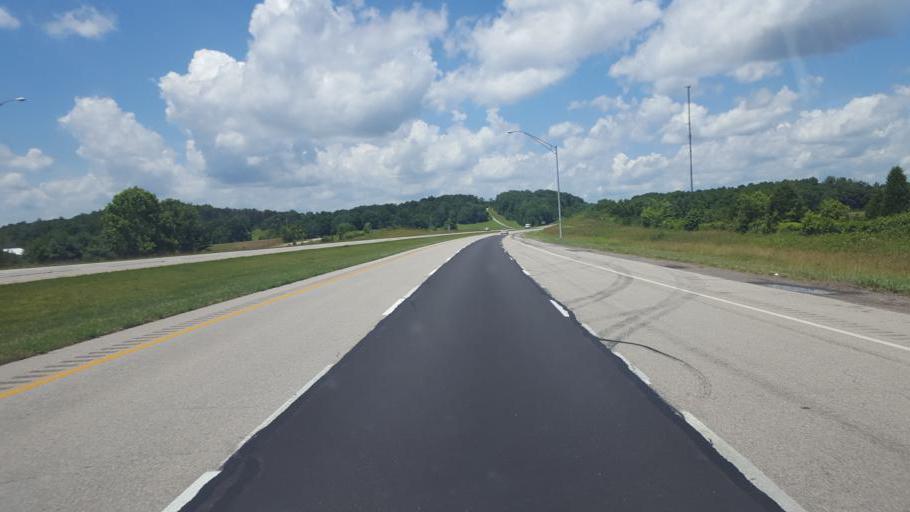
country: US
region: Ohio
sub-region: Gallia County
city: Gallipolis
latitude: 38.8838
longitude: -82.3380
